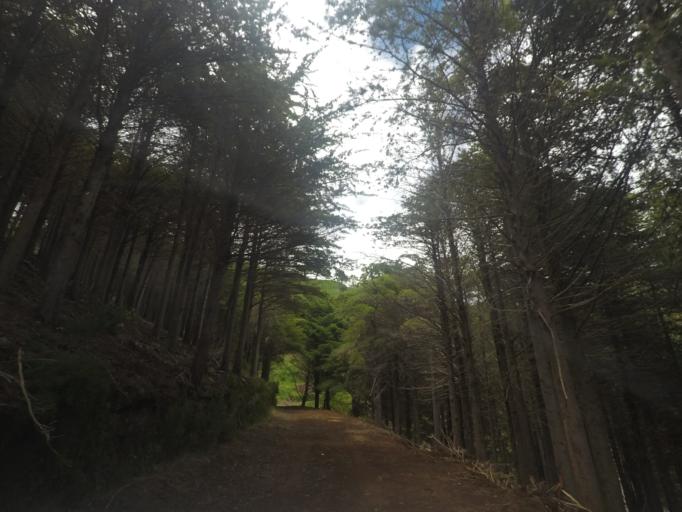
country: PT
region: Madeira
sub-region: Funchal
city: Nossa Senhora do Monte
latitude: 32.7059
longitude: -16.9039
